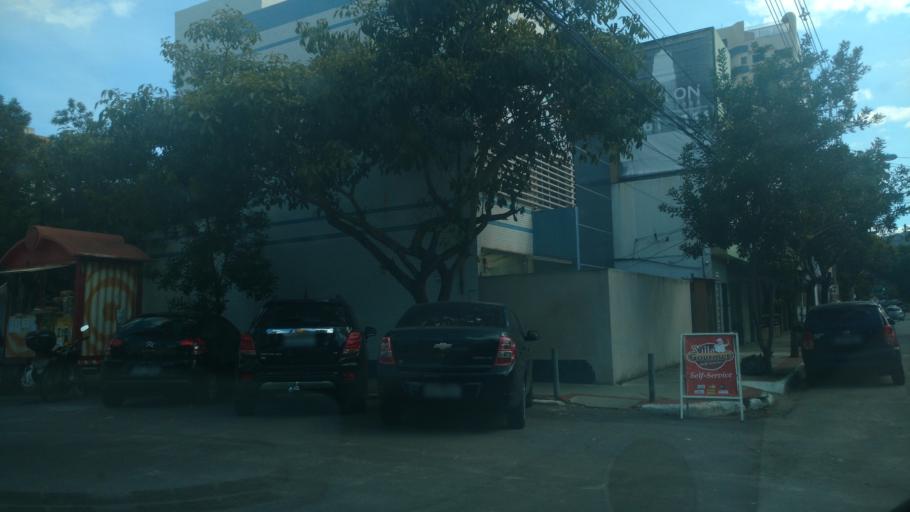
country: BR
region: Espirito Santo
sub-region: Vila Velha
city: Vila Velha
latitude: -20.3340
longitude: -40.2878
